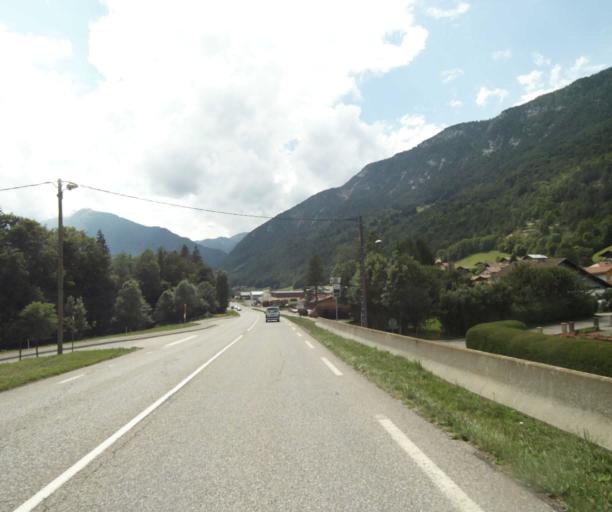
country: FR
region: Rhone-Alpes
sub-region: Departement de la Haute-Savoie
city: Thones
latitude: 45.8985
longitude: 6.3469
